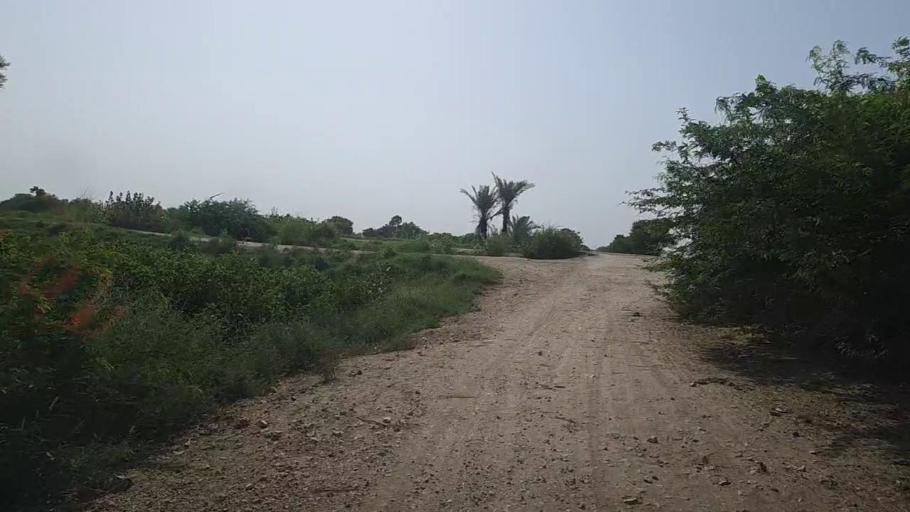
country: PK
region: Sindh
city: Pad Idan
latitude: 26.7650
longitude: 68.3268
